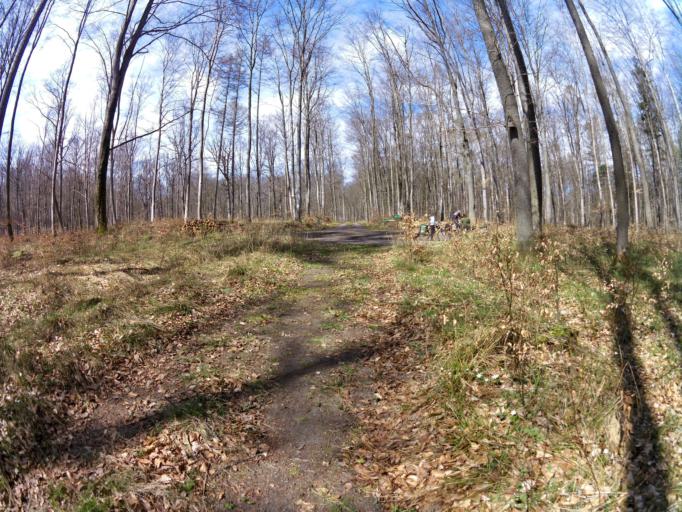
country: PL
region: West Pomeranian Voivodeship
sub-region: Powiat szczecinecki
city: Szczecinek
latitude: 53.7845
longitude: 16.6170
